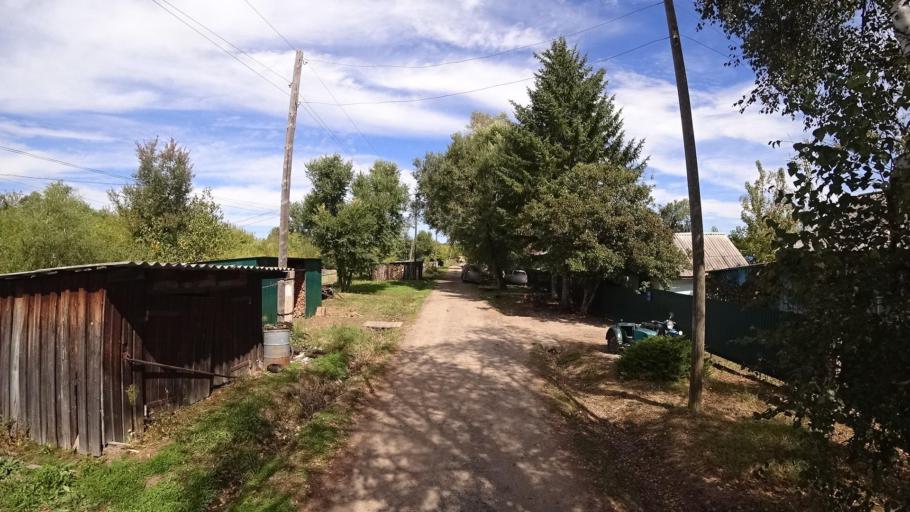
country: RU
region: Primorskiy
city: Yakovlevka
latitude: 44.6437
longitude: 133.5956
